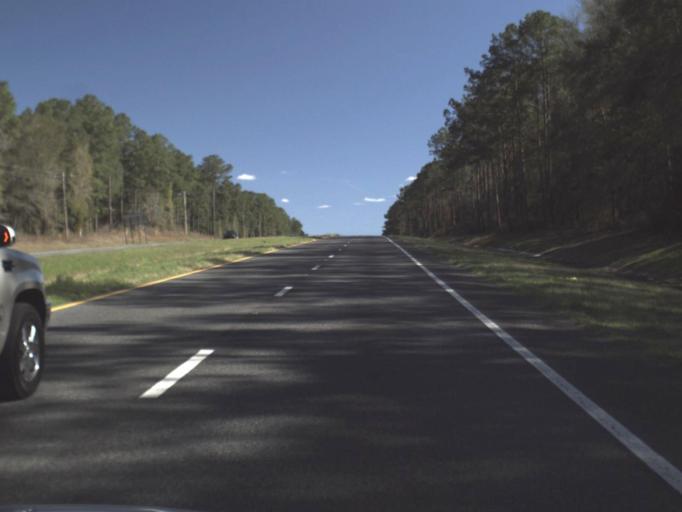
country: US
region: Florida
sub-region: Gadsden County
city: Midway
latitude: 30.5442
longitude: -84.4831
